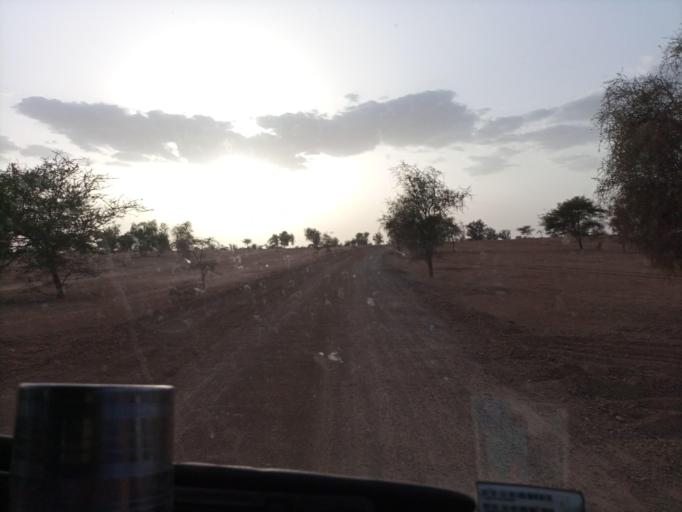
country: SN
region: Louga
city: Dara
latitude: 15.3761
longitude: -15.5906
